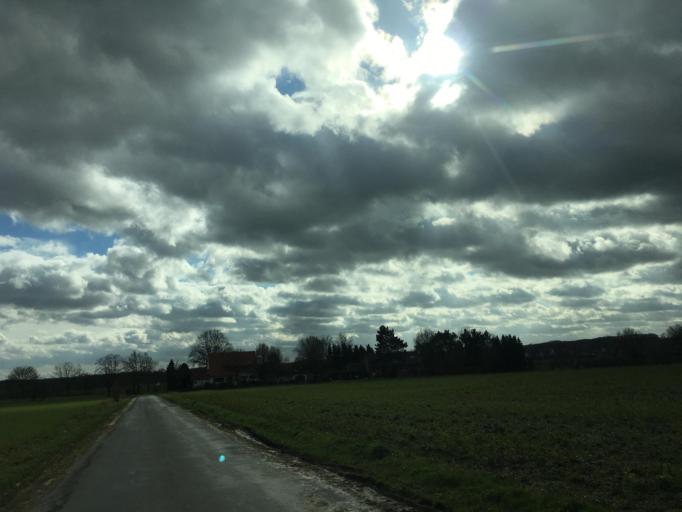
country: DE
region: North Rhine-Westphalia
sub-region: Regierungsbezirk Munster
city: Horstmar
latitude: 52.0879
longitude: 7.3159
